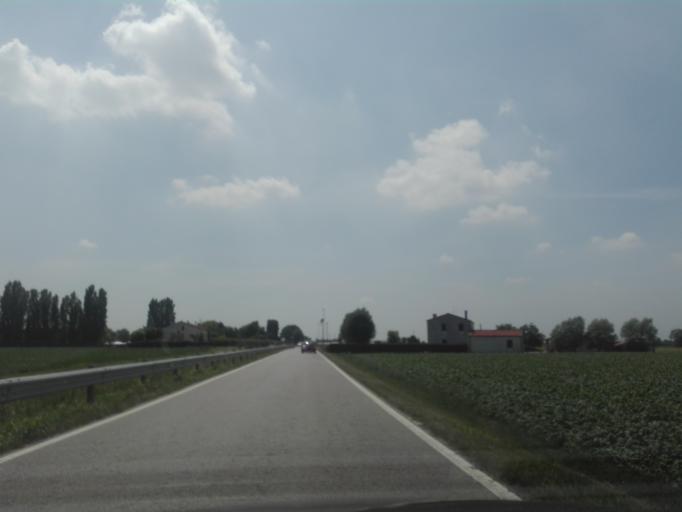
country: IT
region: Veneto
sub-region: Provincia di Rovigo
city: Grignano Polesine
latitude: 45.0361
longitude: 11.7265
